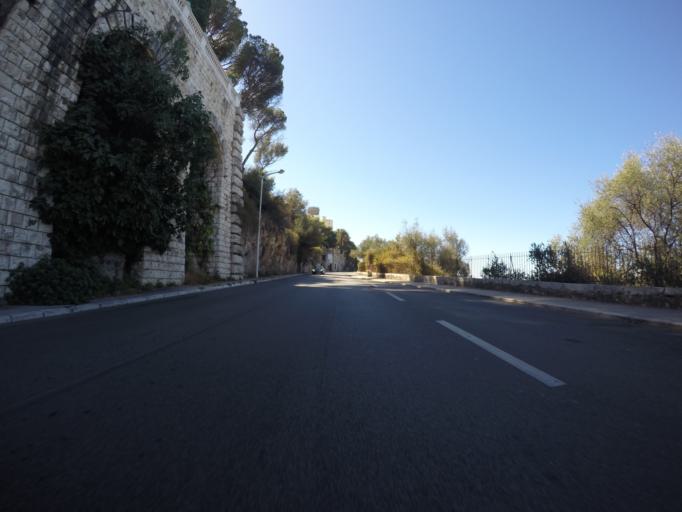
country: FR
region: Provence-Alpes-Cote d'Azur
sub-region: Departement des Alpes-Maritimes
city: Villefranche-sur-Mer
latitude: 43.6909
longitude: 7.2952
